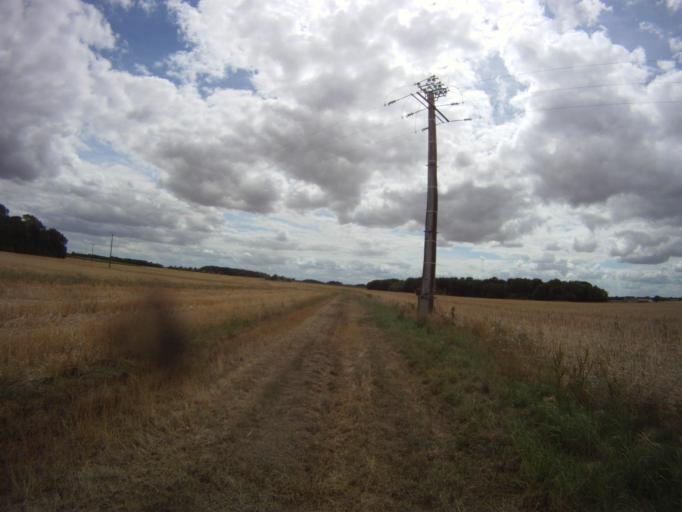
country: FR
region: Centre
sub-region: Departement du Loir-et-Cher
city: Montoire-sur-le-Loir
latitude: 47.6931
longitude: 0.8115
